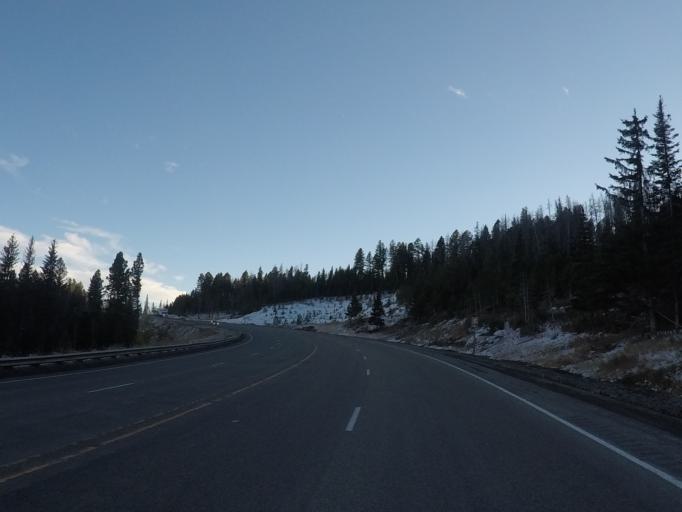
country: US
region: Montana
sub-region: Lewis and Clark County
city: Helena West Side
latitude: 46.5677
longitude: -112.3060
